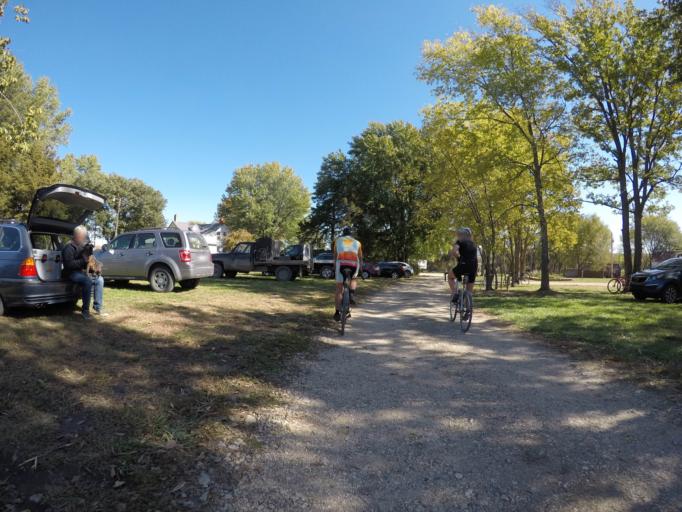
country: US
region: Kansas
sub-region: Wabaunsee County
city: Alma
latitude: 38.9451
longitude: -96.4049
